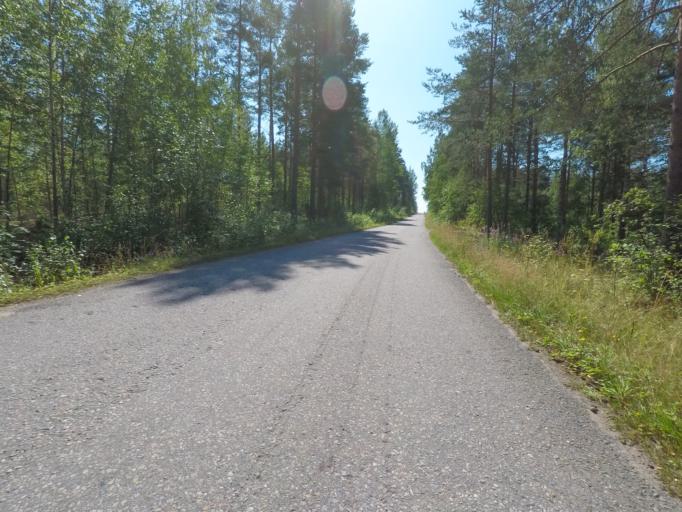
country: FI
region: Southern Savonia
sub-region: Mikkeli
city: Puumala
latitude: 61.4196
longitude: 28.0933
